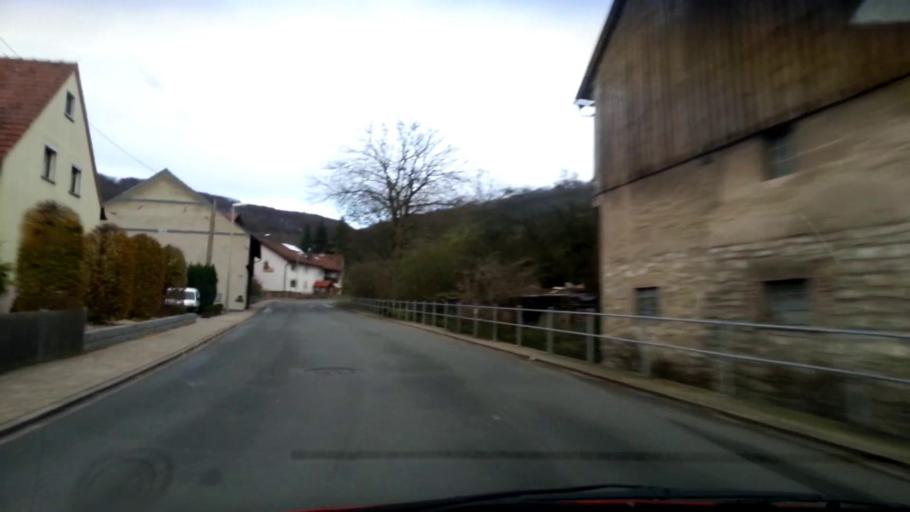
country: DE
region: Bavaria
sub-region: Upper Franconia
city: Poxdorf
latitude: 49.9182
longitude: 11.0750
